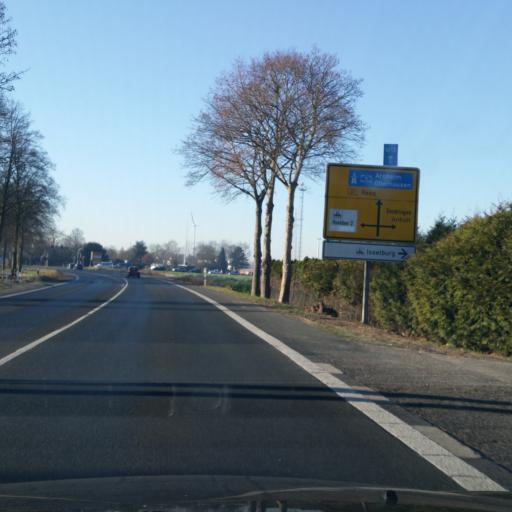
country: DE
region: North Rhine-Westphalia
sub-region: Regierungsbezirk Munster
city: Isselburg
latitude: 51.8208
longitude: 6.4474
